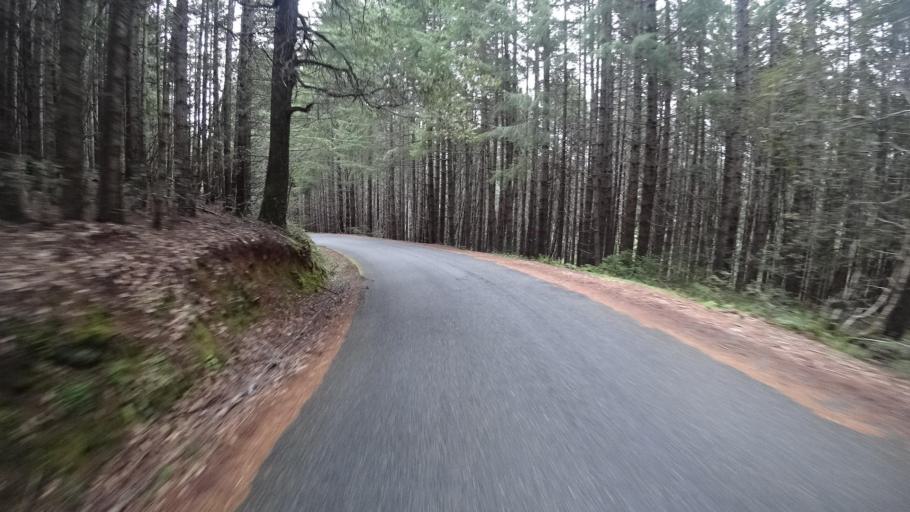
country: US
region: California
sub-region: Humboldt County
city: Willow Creek
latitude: 41.2004
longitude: -123.7756
